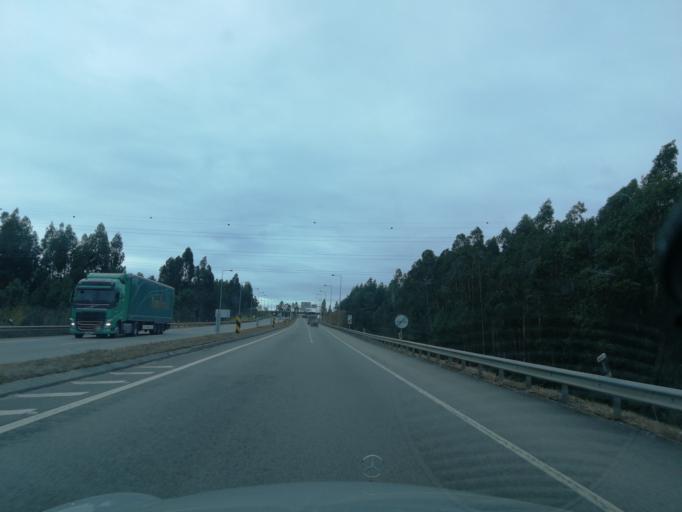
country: PT
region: Aveiro
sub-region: Agueda
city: Valongo
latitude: 40.6007
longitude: -8.4679
